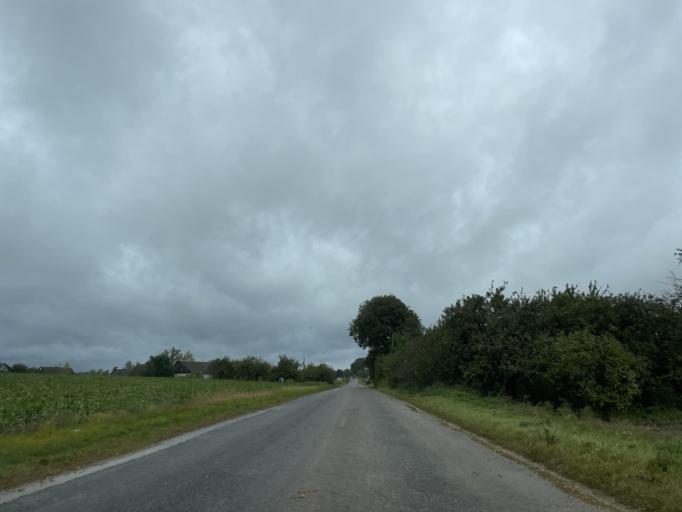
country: BY
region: Brest
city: Lyakhavichy
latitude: 53.1897
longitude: 26.2504
